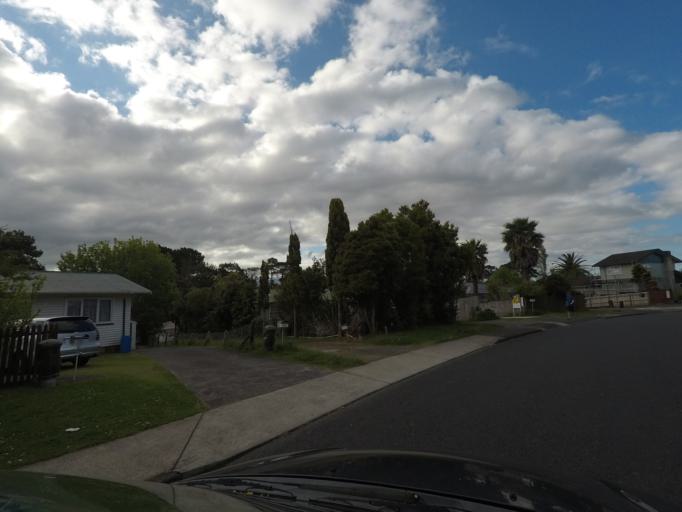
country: NZ
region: Auckland
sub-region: Auckland
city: Rosebank
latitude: -36.8879
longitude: 174.6535
